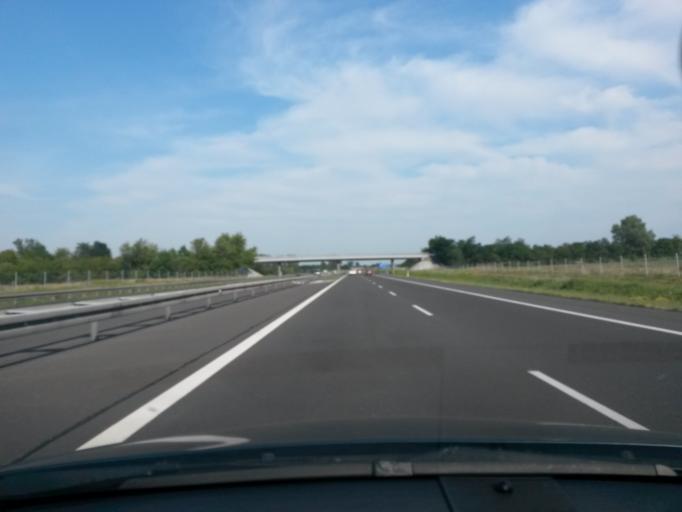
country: PL
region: Greater Poland Voivodeship
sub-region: Powiat slupecki
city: Strzalkowo
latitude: 52.2631
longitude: 17.7643
